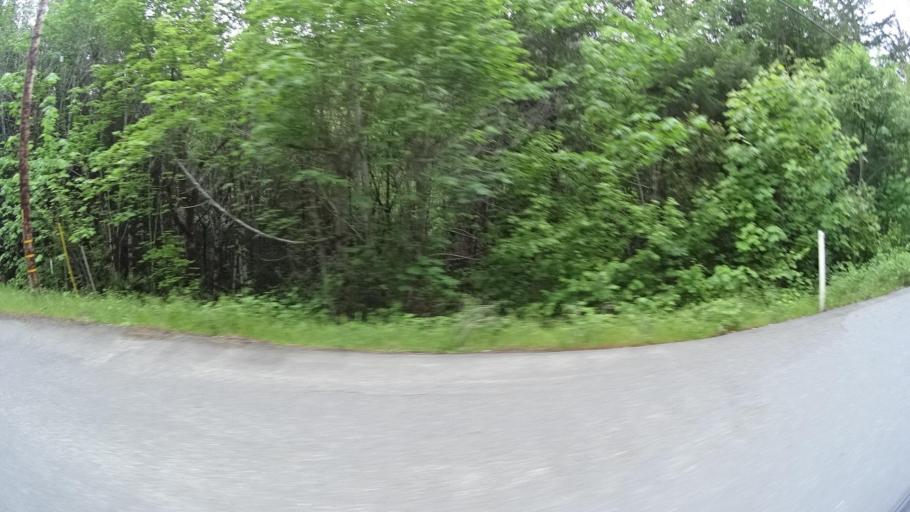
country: US
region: California
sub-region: Humboldt County
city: Willow Creek
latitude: 41.2036
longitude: -123.7520
